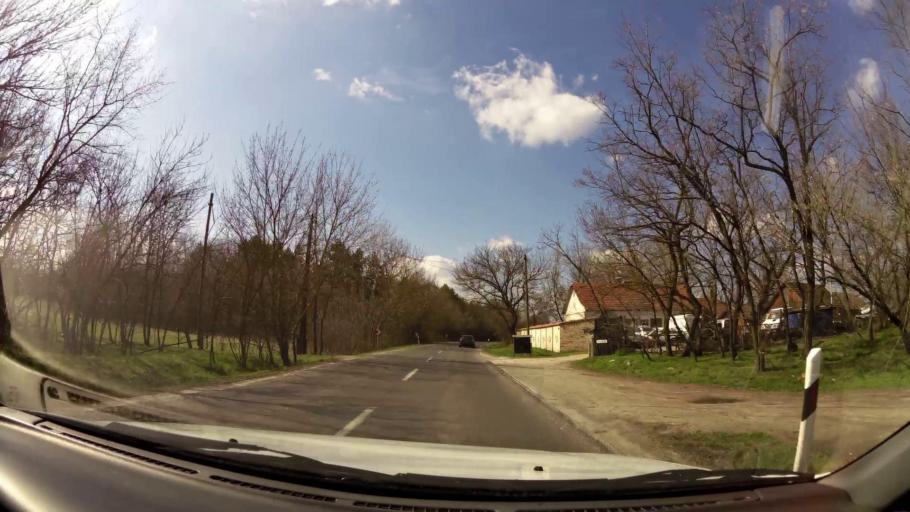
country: HU
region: Pest
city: Farmos
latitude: 47.3586
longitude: 19.8185
